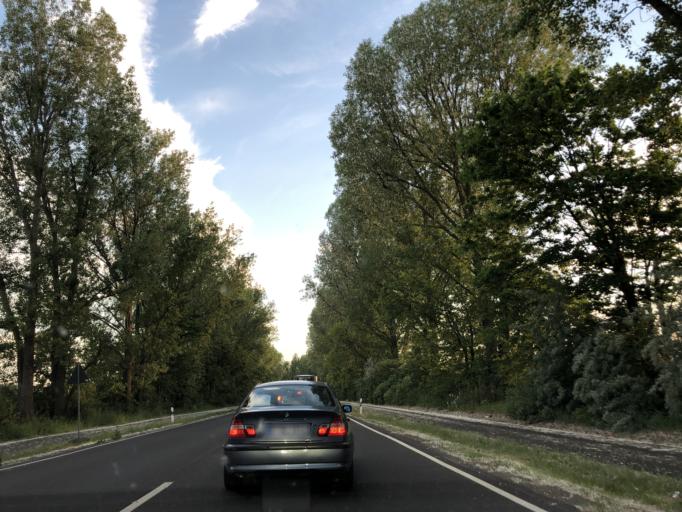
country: DE
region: Berlin
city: Stadtrandsiedlung Malchow
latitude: 52.5914
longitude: 13.4920
